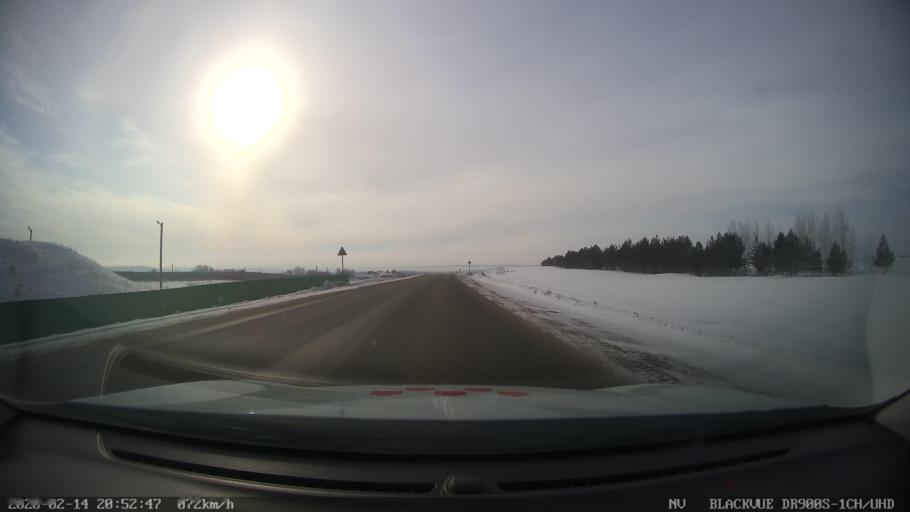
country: RU
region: Tatarstan
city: Kuybyshevskiy Zaton
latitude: 55.2009
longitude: 49.2497
